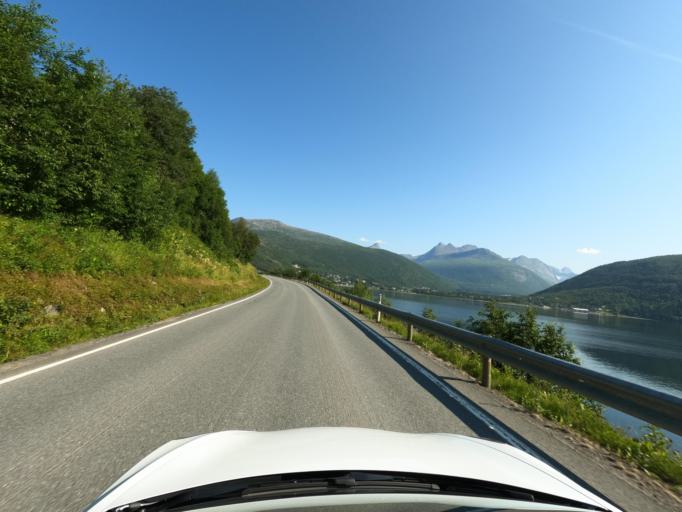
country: NO
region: Nordland
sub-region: Narvik
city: Narvik
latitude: 68.3848
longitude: 17.5677
